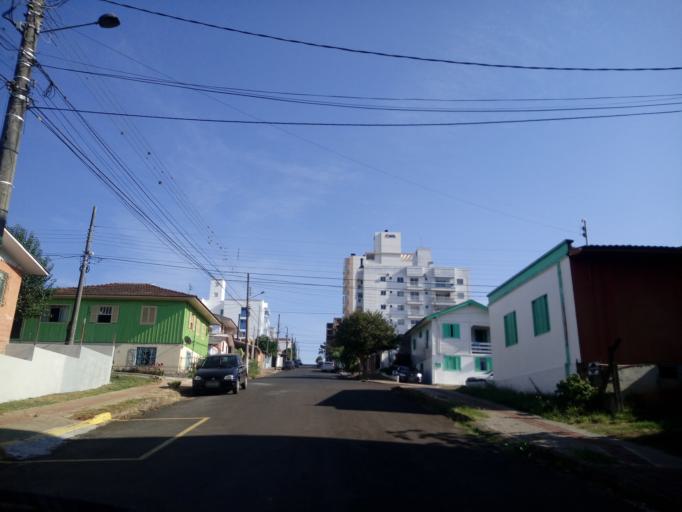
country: BR
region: Santa Catarina
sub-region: Chapeco
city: Chapeco
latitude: -27.0953
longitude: -52.6292
